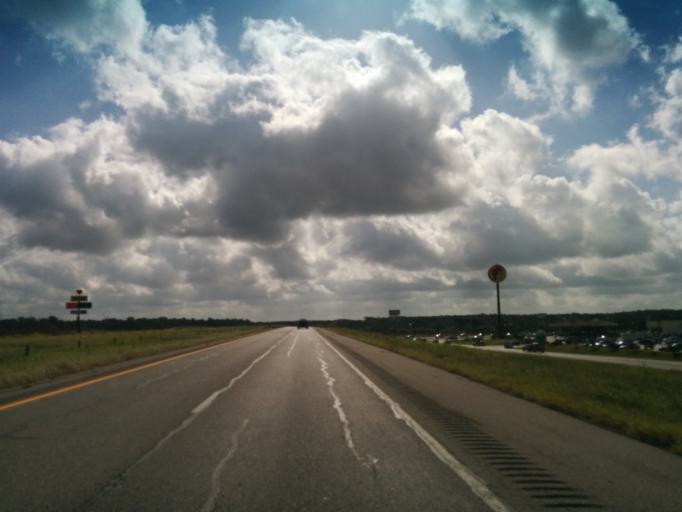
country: US
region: Texas
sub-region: Caldwell County
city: Luling
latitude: 29.6518
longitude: -97.5954
